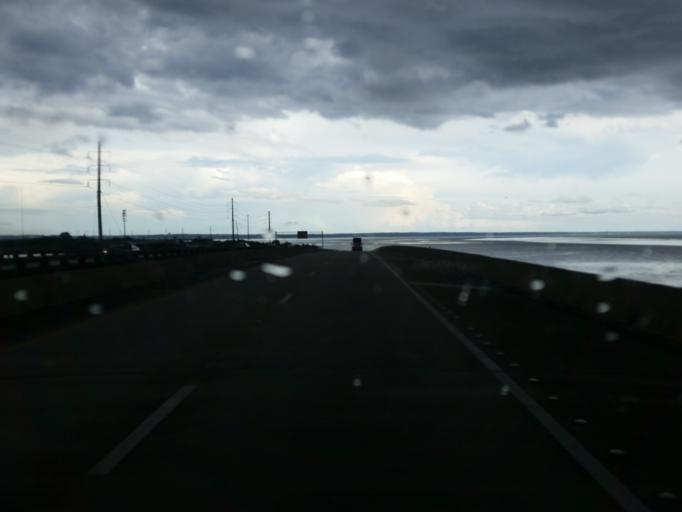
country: US
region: Alabama
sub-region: Mobile County
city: Mobile
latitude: 30.6839
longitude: -88.0093
